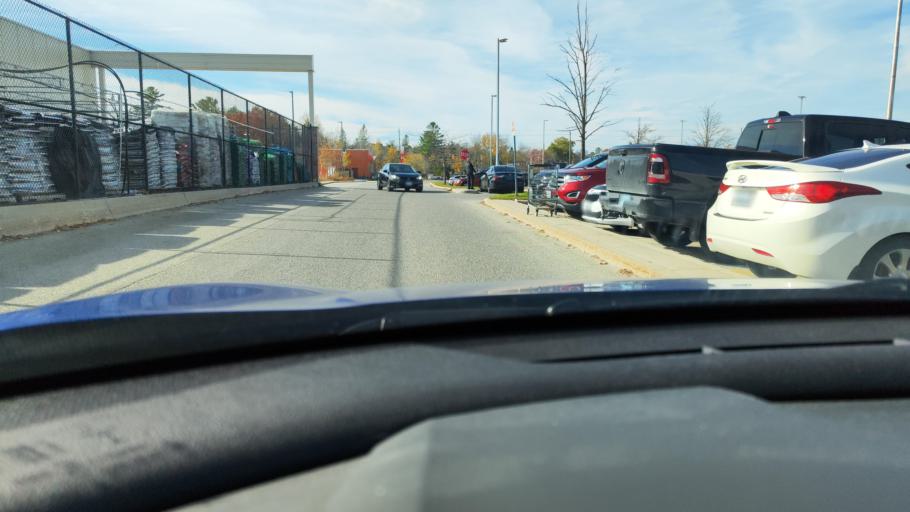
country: CA
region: Ontario
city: Wasaga Beach
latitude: 44.4725
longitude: -80.0737
